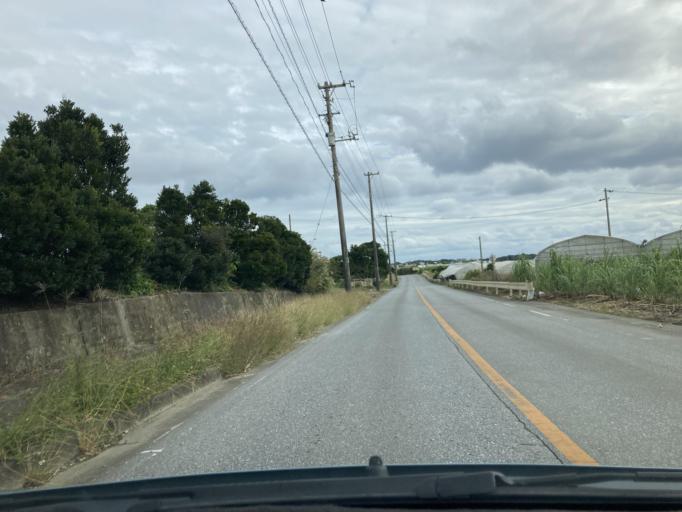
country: JP
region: Okinawa
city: Itoman
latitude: 26.1157
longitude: 127.6973
